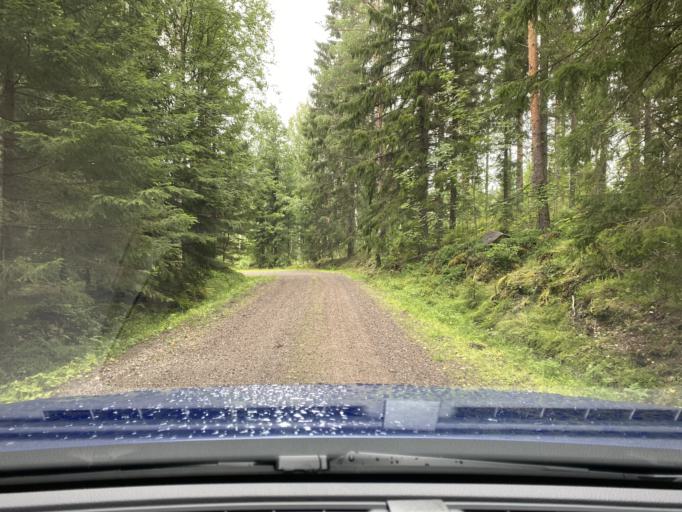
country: FI
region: Pirkanmaa
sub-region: Ylae-Pirkanmaa
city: Maenttae
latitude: 62.0189
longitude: 24.7567
